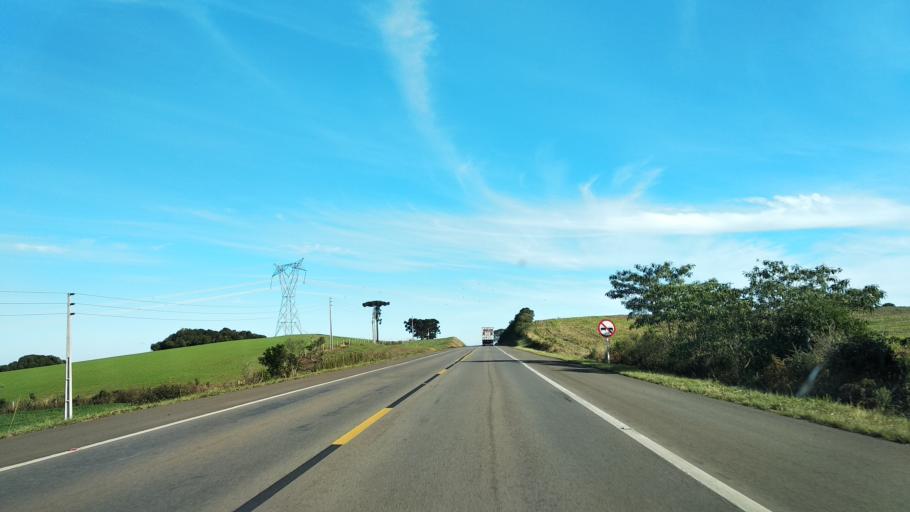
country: BR
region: Santa Catarina
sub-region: Celso Ramos
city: Celso Ramos
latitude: -27.5033
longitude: -51.3434
